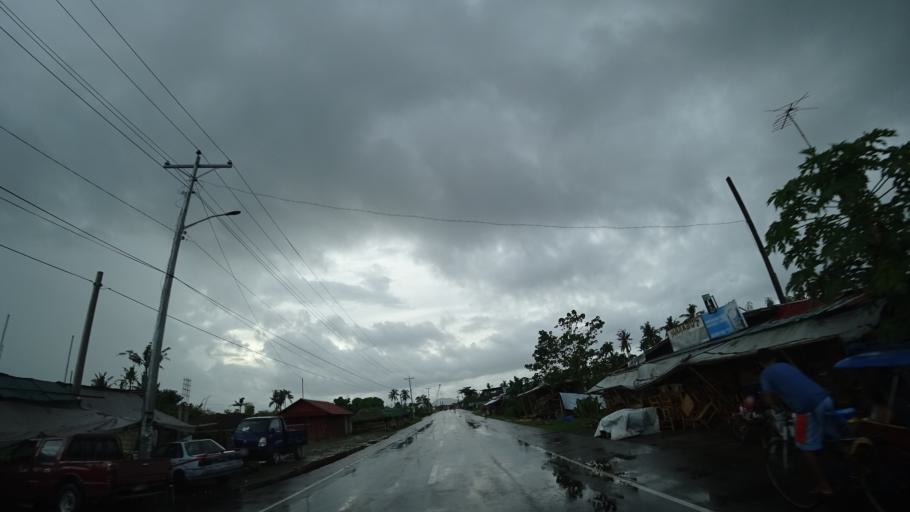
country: PH
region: Eastern Visayas
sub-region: Province of Leyte
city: Tanauan
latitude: 11.1179
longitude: 125.0172
